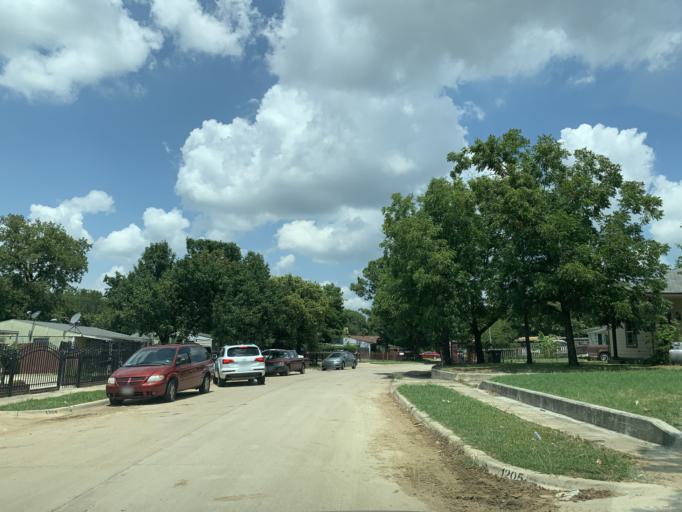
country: US
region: Texas
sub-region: Tarrant County
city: Fort Worth
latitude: 32.7321
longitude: -97.2633
